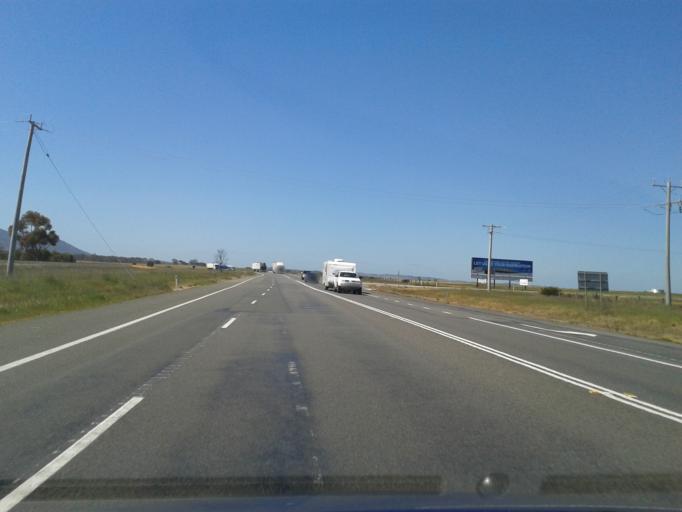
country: AU
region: Victoria
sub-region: Ararat
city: Ararat
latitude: -37.3040
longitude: 142.9875
